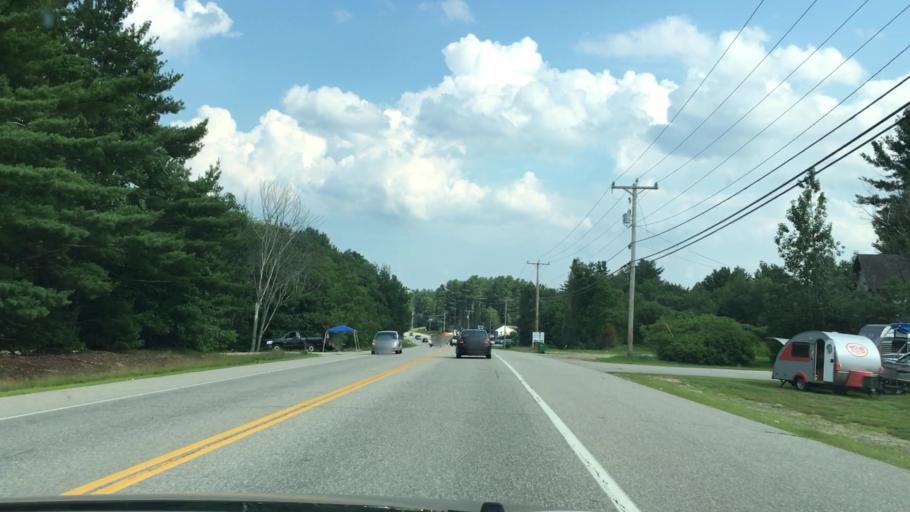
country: US
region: New Hampshire
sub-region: Strafford County
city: Rochester
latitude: 43.3429
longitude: -71.0201
